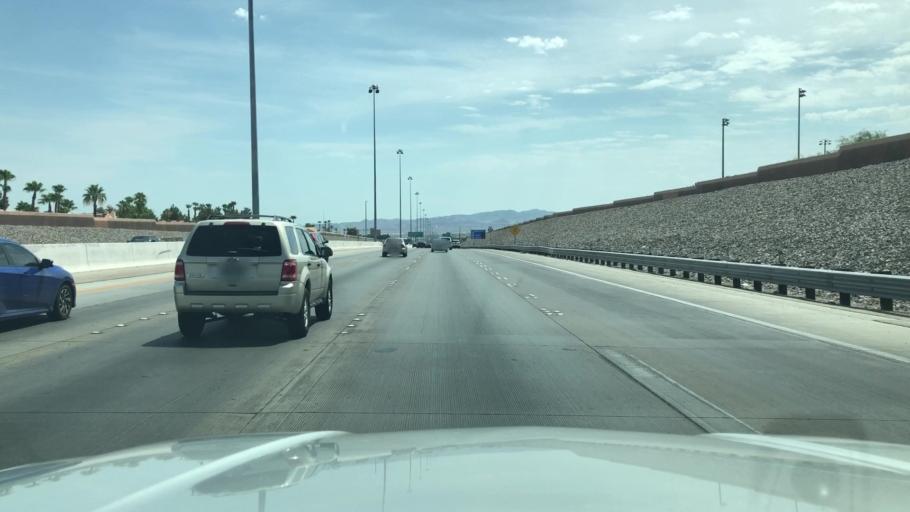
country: US
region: Nevada
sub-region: Clark County
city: Whitney
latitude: 36.0252
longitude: -115.0789
